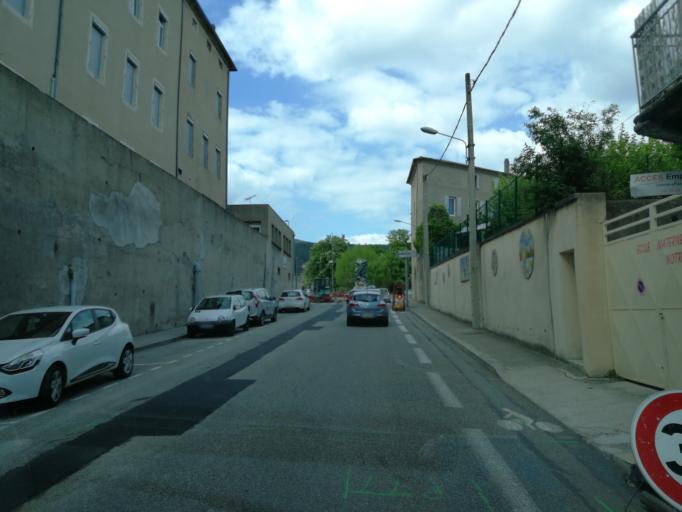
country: FR
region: Rhone-Alpes
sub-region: Departement de l'Ardeche
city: Privas
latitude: 44.7354
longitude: 4.6014
